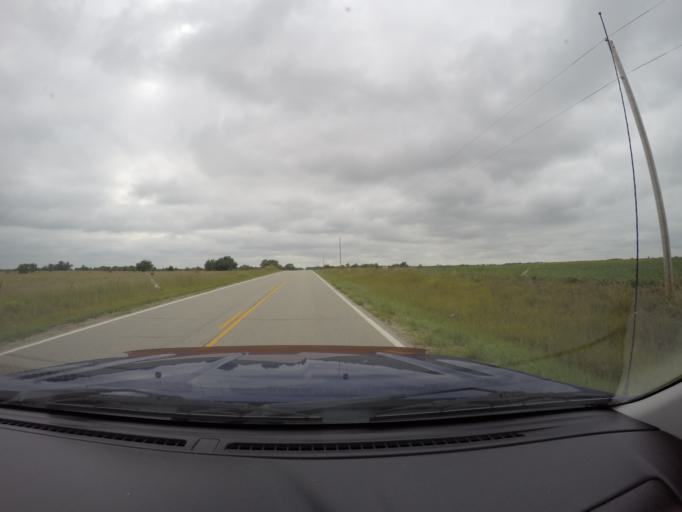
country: US
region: Kansas
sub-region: Morris County
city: Council Grove
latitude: 38.7977
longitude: -96.6759
